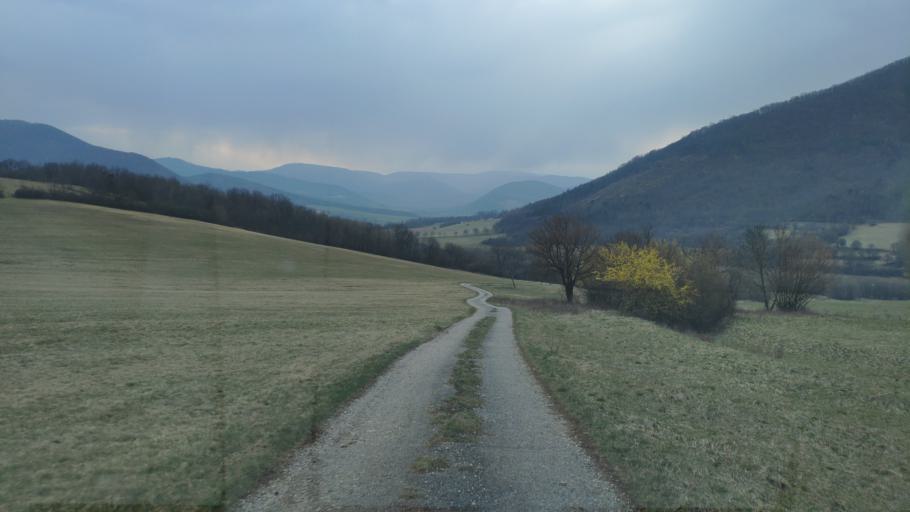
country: SK
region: Kosicky
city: Roznava
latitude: 48.6552
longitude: 20.3900
